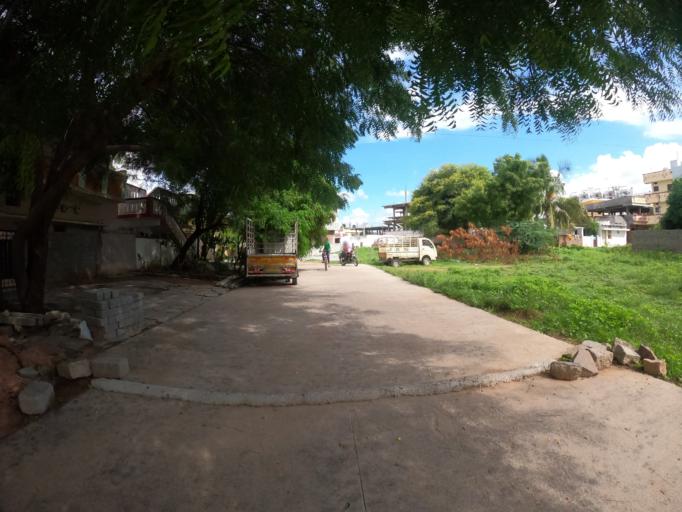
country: IN
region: Telangana
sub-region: Hyderabad
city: Hyderabad
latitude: 17.3531
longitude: 78.3905
